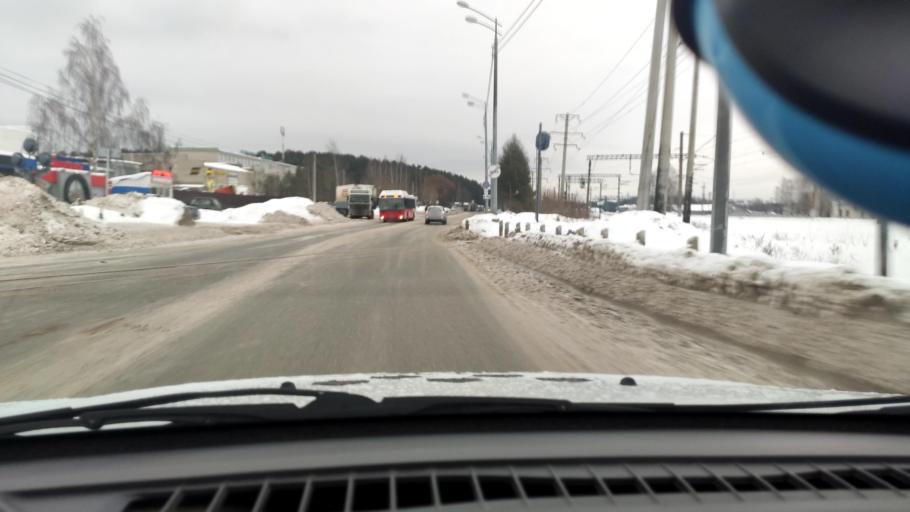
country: RU
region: Perm
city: Kondratovo
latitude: 58.0398
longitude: 56.1631
